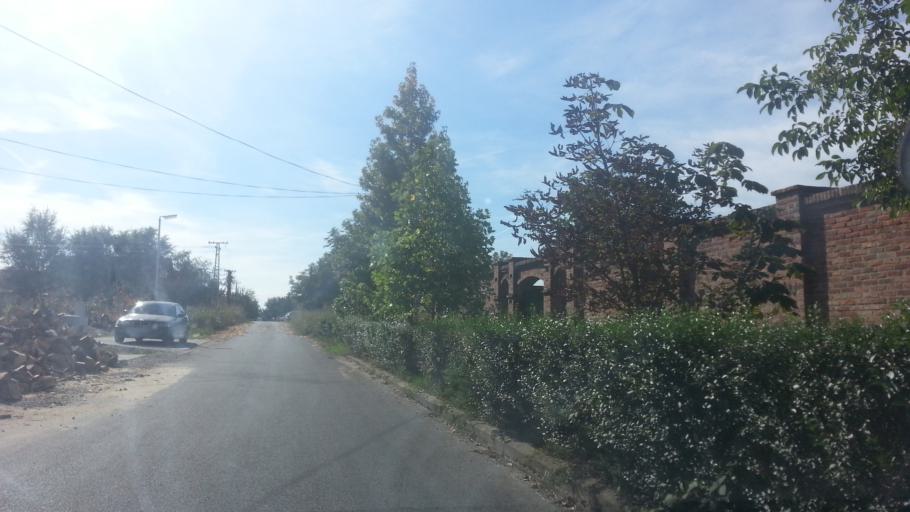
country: RS
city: Novi Banovci
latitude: 44.9685
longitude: 20.2728
